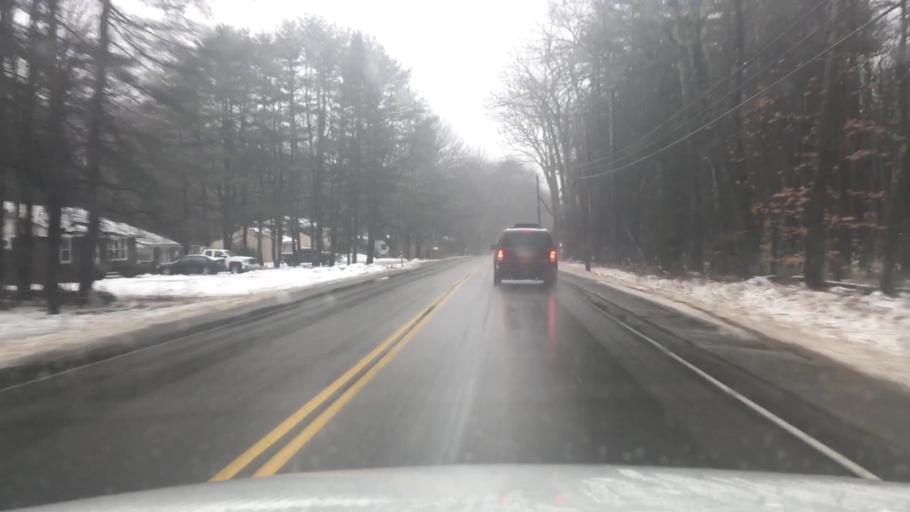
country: US
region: Maine
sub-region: Cumberland County
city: Westbrook
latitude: 43.6383
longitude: -70.3960
